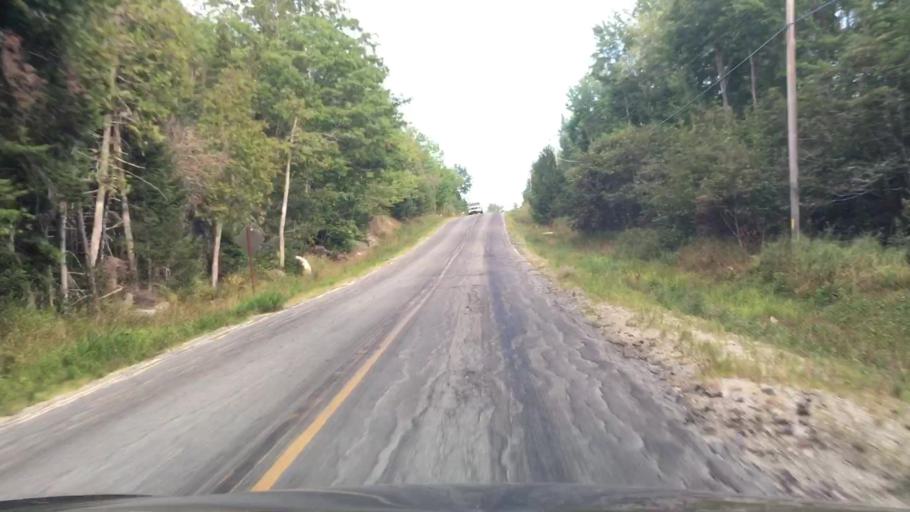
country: US
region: Maine
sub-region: Hancock County
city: Surry
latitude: 44.5060
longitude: -68.5923
